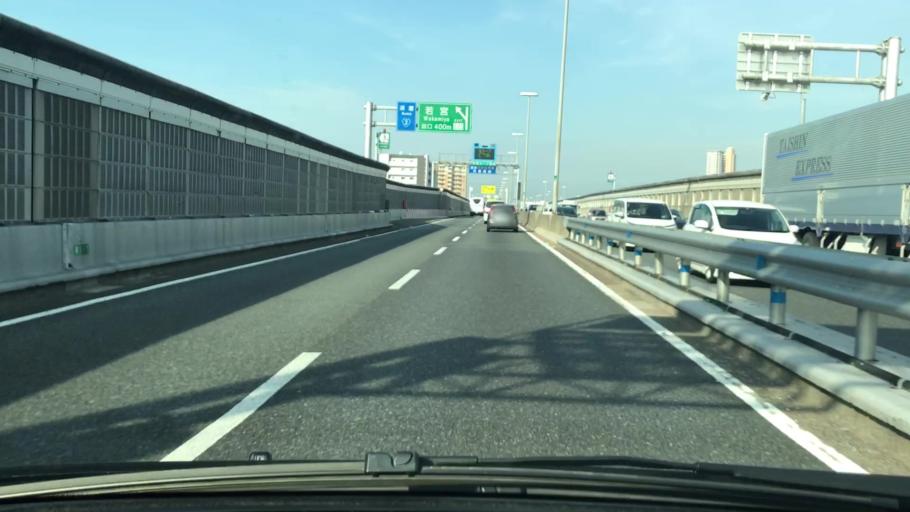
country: JP
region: Hyogo
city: Kobe
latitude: 34.6500
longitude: 135.1388
